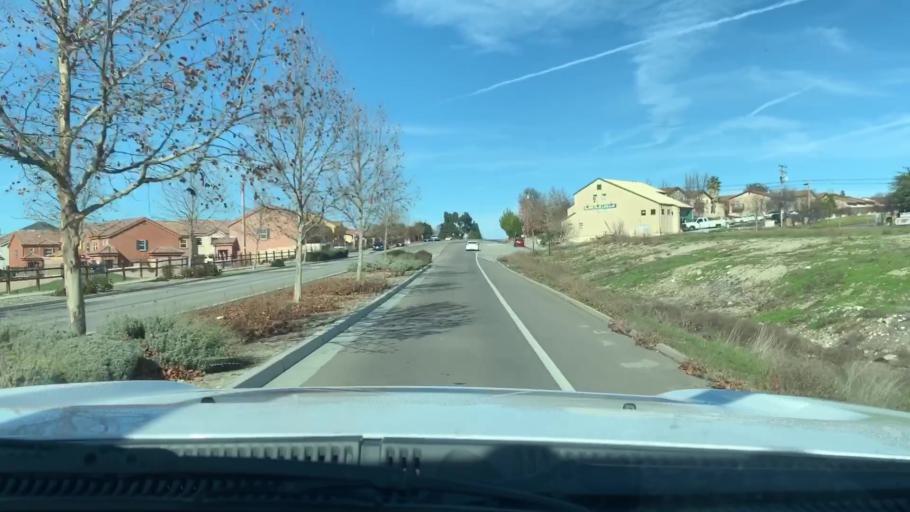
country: US
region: California
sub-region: San Luis Obispo County
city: Atascadero
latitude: 35.4536
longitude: -120.6384
